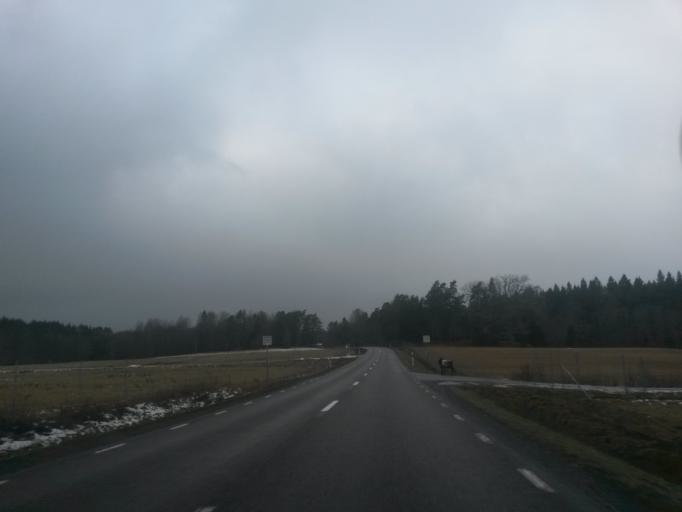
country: SE
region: Vaestra Goetaland
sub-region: Alingsas Kommun
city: Sollebrunn
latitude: 58.1367
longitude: 12.4525
